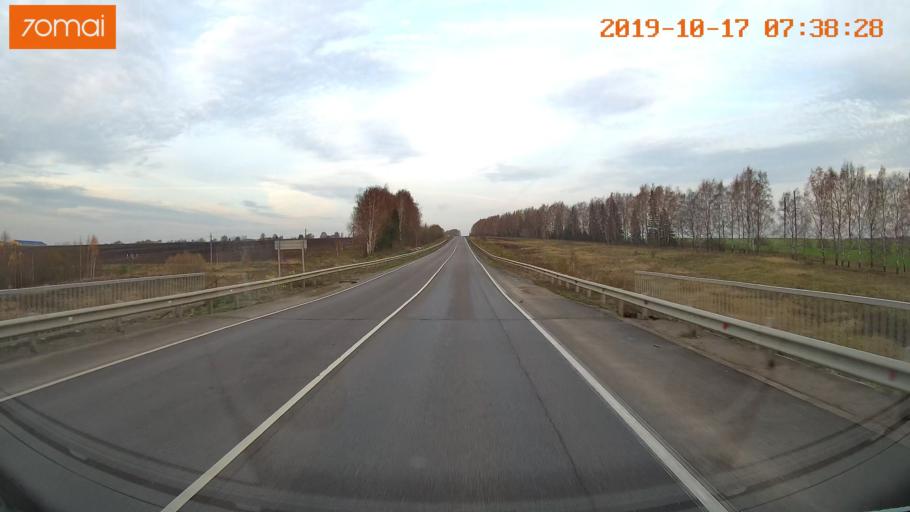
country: RU
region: Vladimir
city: Yur'yev-Pol'skiy
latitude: 56.4559
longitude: 39.8734
